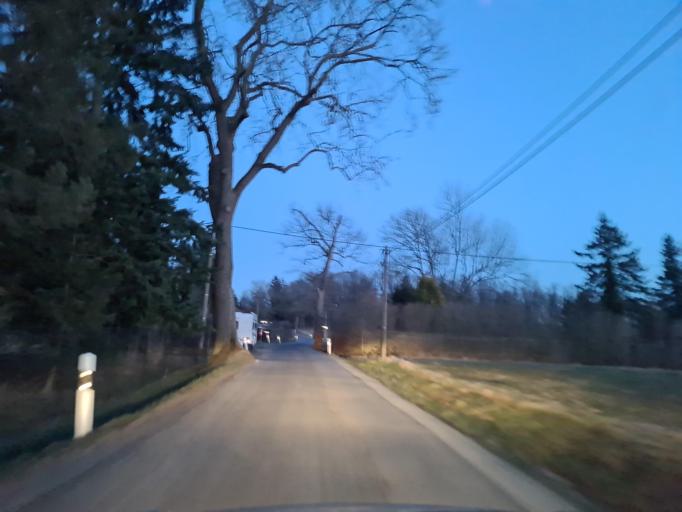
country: DE
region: Saxony
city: Plauen
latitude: 50.5177
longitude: 12.1068
